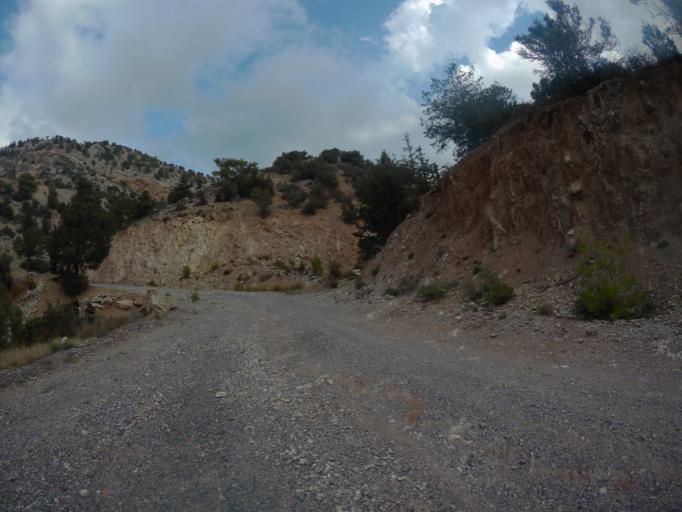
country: CY
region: Ammochostos
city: Lefkonoiko
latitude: 35.3460
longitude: 33.7257
